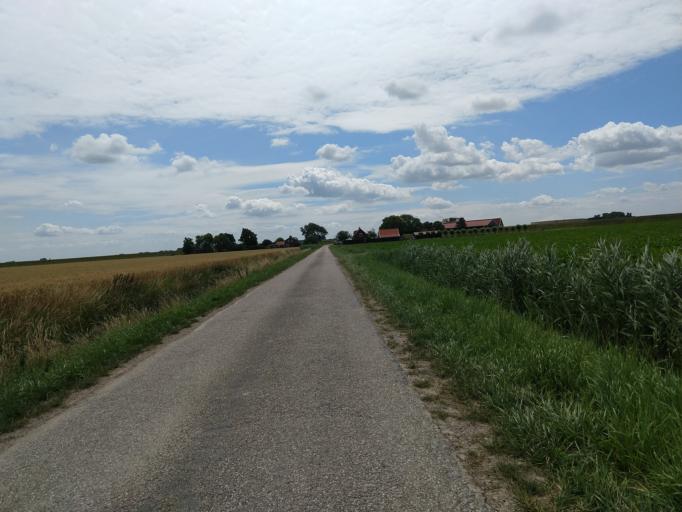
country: NL
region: Zeeland
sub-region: Gemeente Noord-Beveland
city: Kamperland
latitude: 51.5250
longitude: 3.7588
